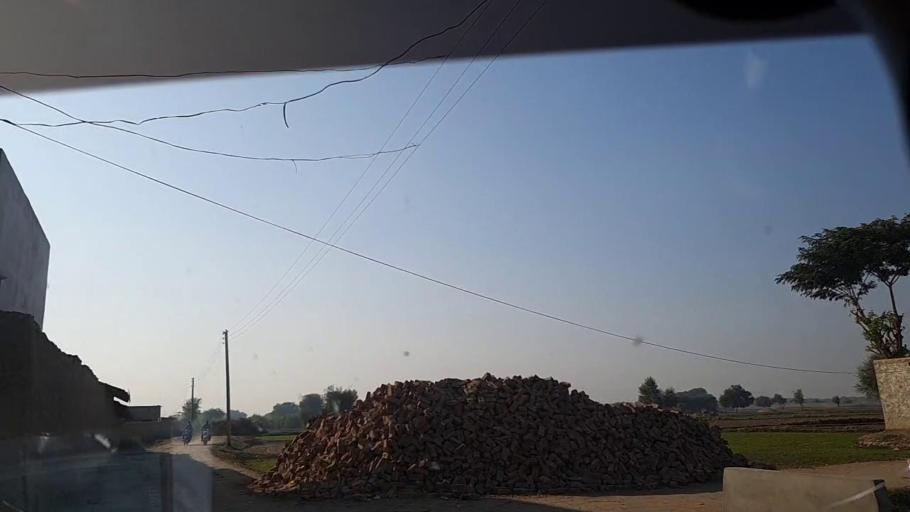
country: PK
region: Sindh
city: Sobhadero
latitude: 27.2348
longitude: 68.2658
